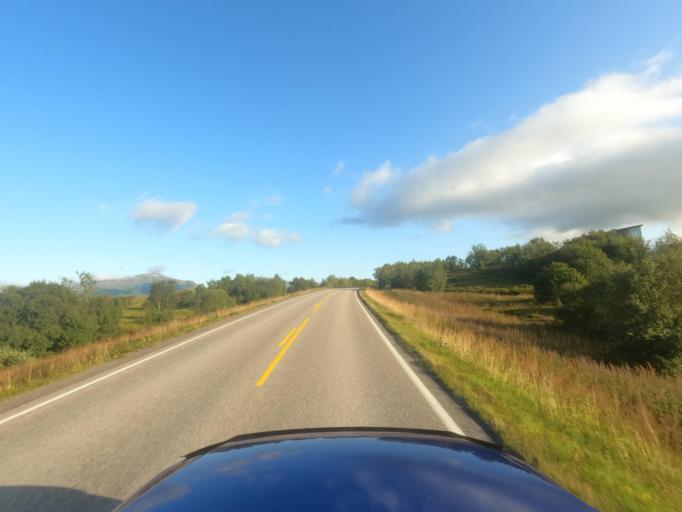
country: NO
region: Nordland
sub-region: Vestvagoy
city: Gravdal
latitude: 68.1499
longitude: 13.5439
